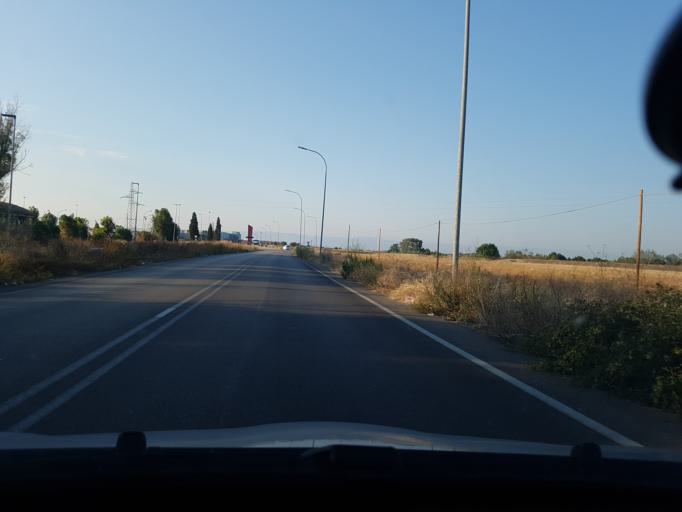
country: IT
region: Apulia
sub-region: Provincia di Foggia
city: Carapelle
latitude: 41.4096
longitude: 15.6531
